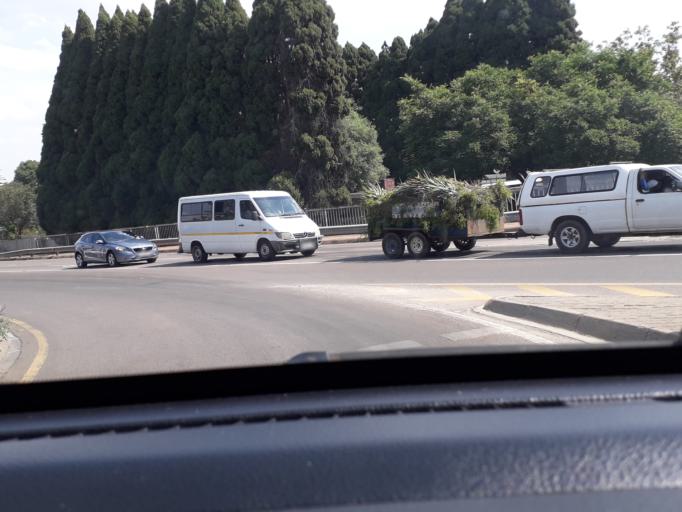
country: ZA
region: Gauteng
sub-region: City of Tshwane Metropolitan Municipality
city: Centurion
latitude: -25.8405
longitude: 28.2118
